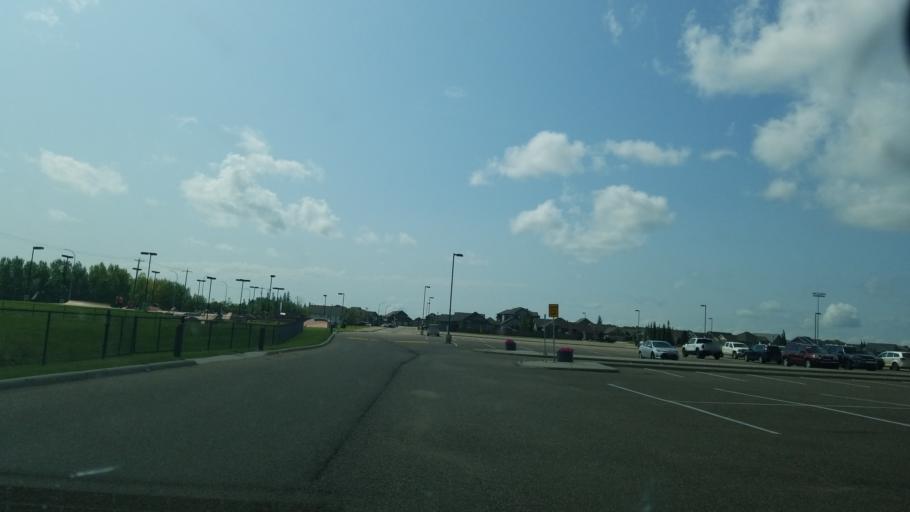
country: CA
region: Saskatchewan
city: Lloydminster
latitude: 53.2497
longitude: -110.0086
